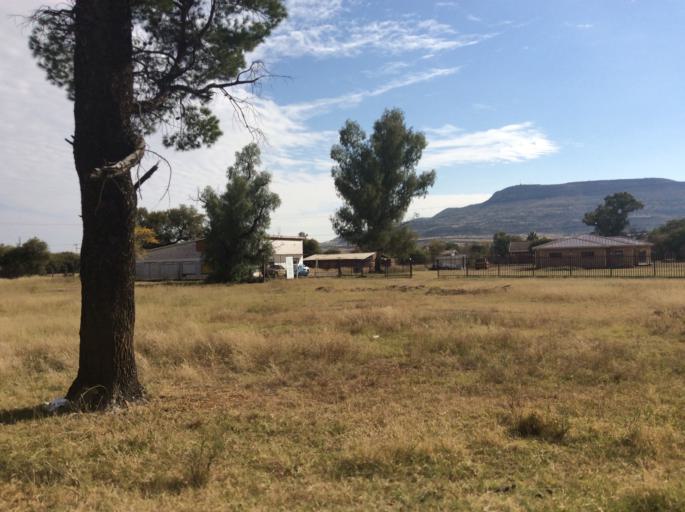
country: LS
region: Mafeteng
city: Mafeteng
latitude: -29.7312
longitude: 27.0271
